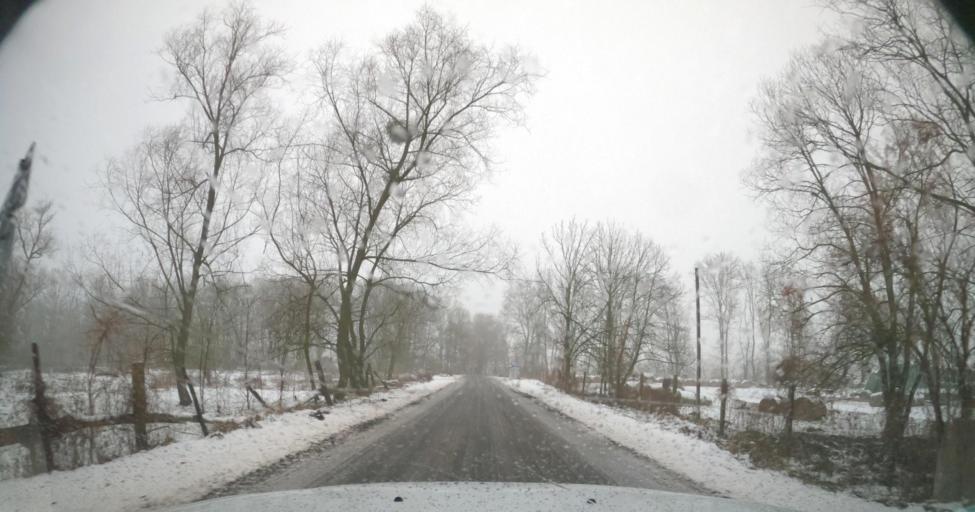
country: PL
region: West Pomeranian Voivodeship
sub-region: Powiat goleniowski
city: Stepnica
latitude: 53.5652
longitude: 14.6817
